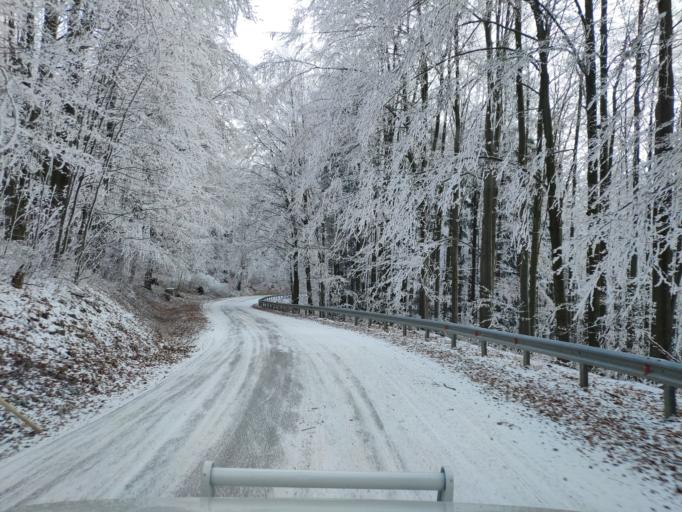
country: SK
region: Kosicky
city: Dobsina
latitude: 48.8062
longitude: 20.4848
